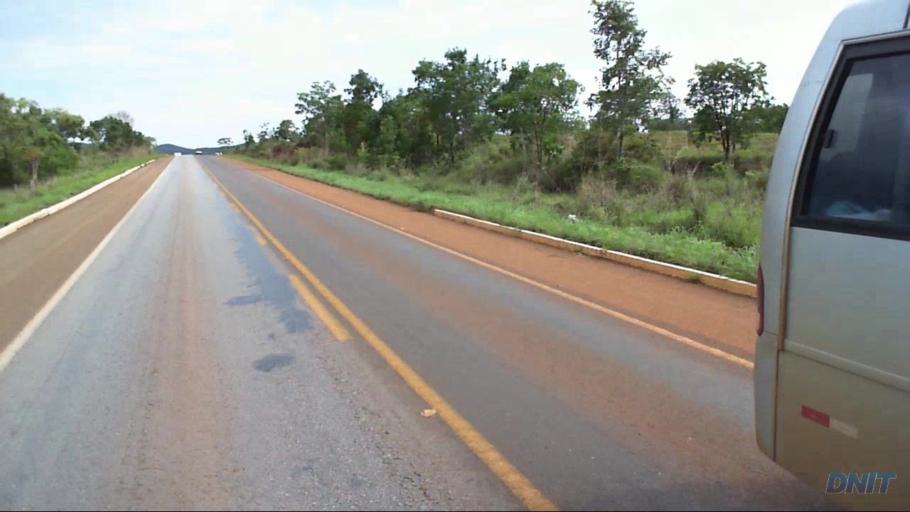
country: BR
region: Goias
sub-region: Barro Alto
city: Barro Alto
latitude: -14.9549
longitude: -48.9322
